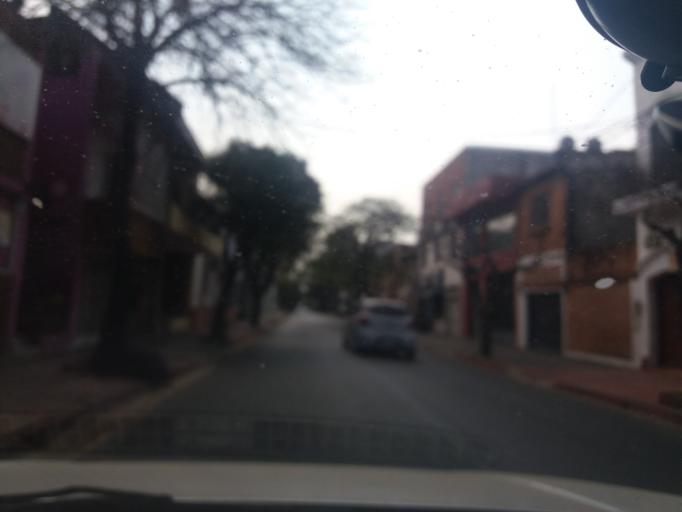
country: AR
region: Corrientes
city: Corrientes
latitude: -27.4740
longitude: -58.8388
